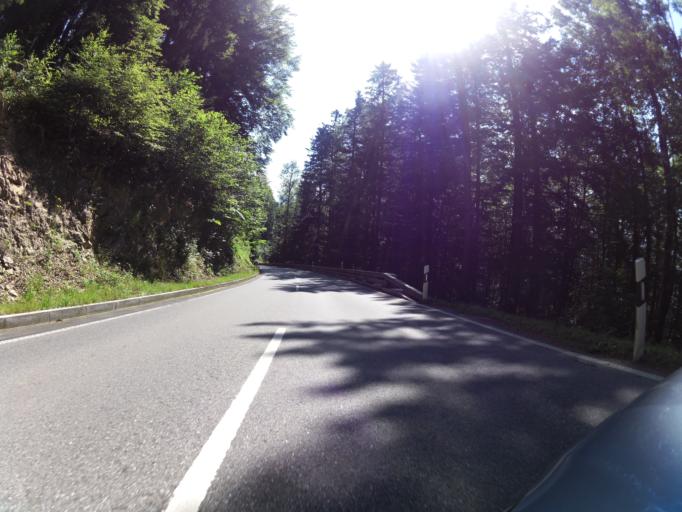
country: DE
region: Bavaria
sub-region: Upper Bavaria
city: Berchtesgaden
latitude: 47.6330
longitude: 13.0314
